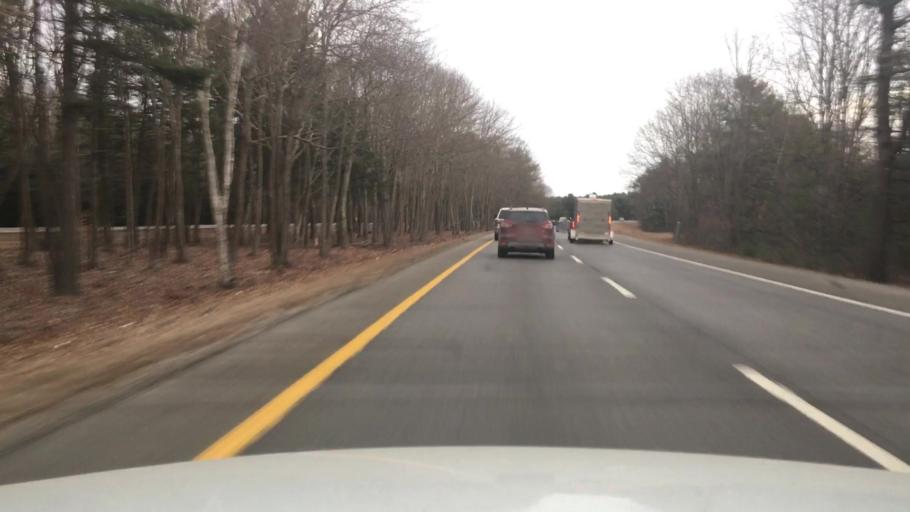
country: US
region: Maine
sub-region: Sagadahoc County
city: Bath
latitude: 43.9176
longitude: -69.8914
